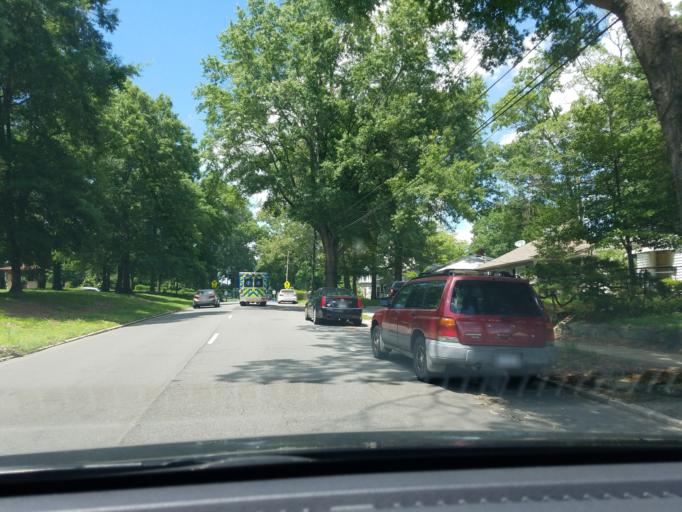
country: US
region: North Carolina
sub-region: Durham County
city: Durham
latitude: 35.9883
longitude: -78.9091
